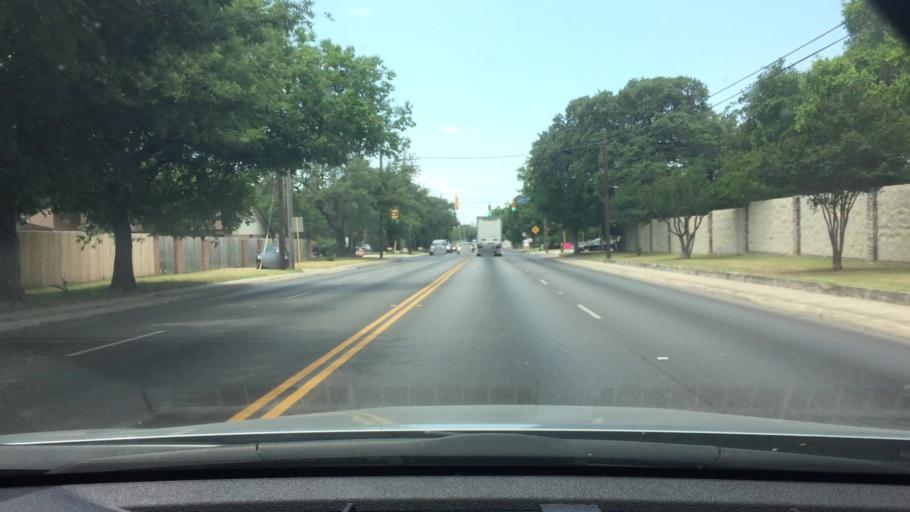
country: US
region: Texas
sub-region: Bexar County
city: Hollywood Park
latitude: 29.5708
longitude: -98.4495
